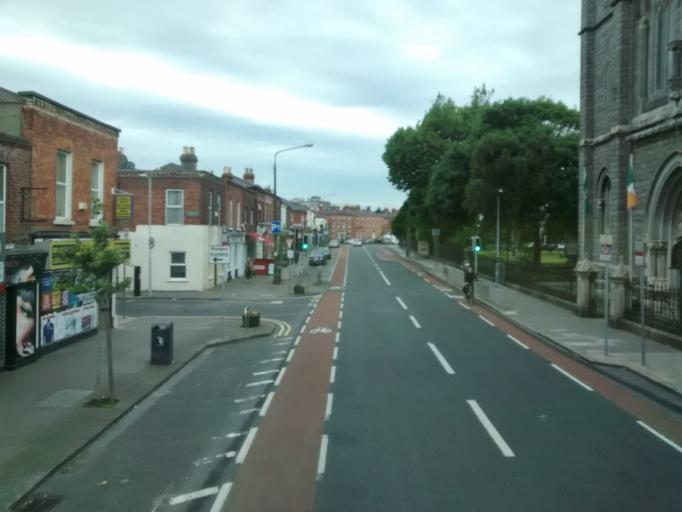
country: IE
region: Leinster
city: Drumcondra
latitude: 53.3578
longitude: -6.2688
